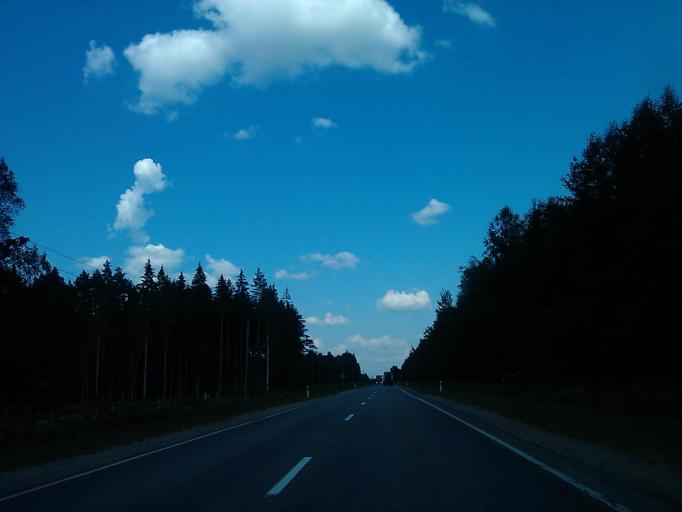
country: LV
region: Skrunda
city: Skrunda
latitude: 56.6613
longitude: 21.9520
